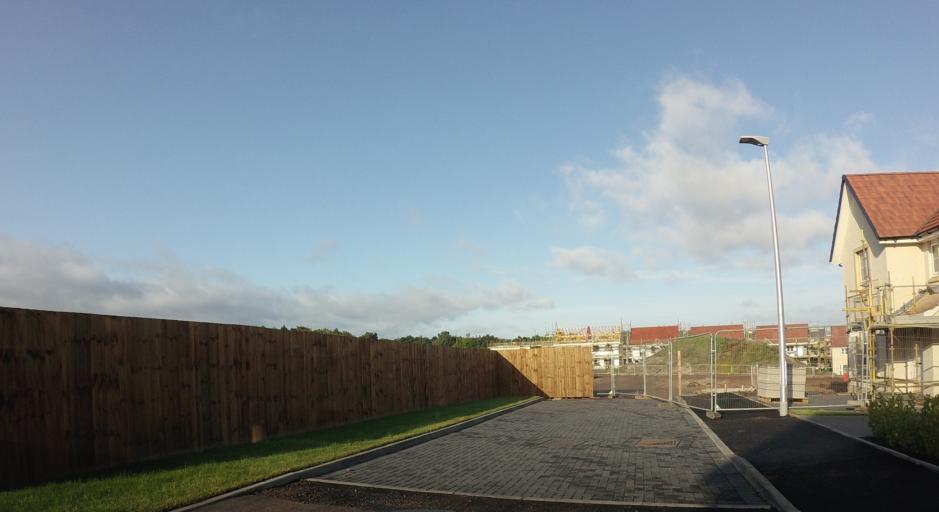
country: GB
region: Scotland
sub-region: East Lothian
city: Musselburgh
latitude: 55.9307
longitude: -3.0185
